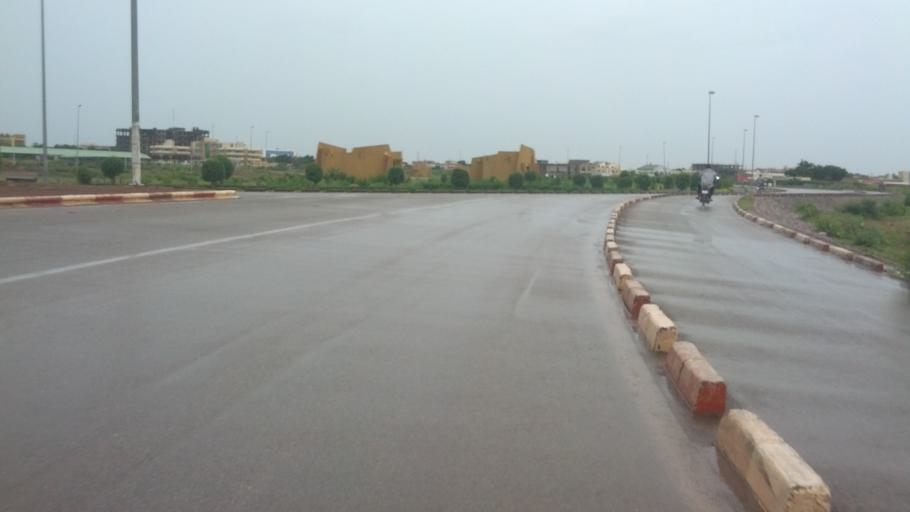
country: BF
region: Centre
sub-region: Kadiogo Province
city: Ouagadougou
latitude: 12.3150
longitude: -1.5029
